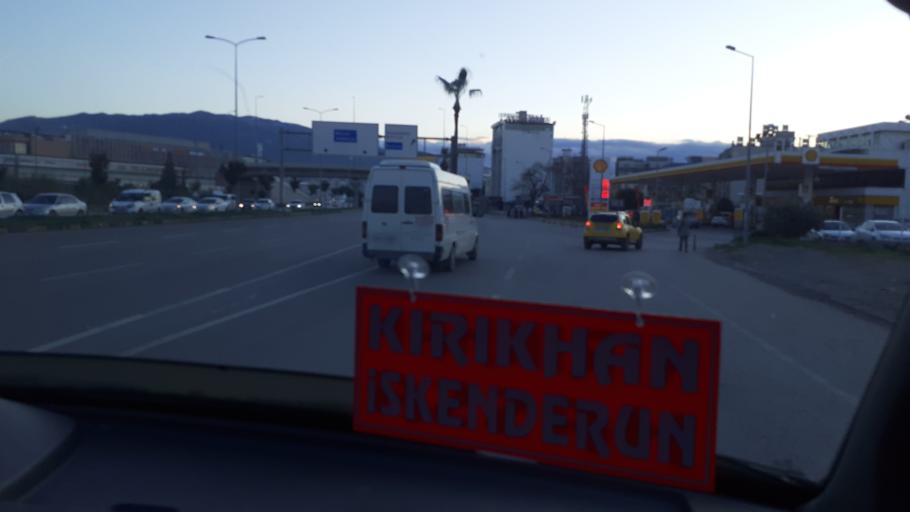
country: TR
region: Hatay
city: Iskenderun
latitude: 36.5795
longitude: 36.1629
